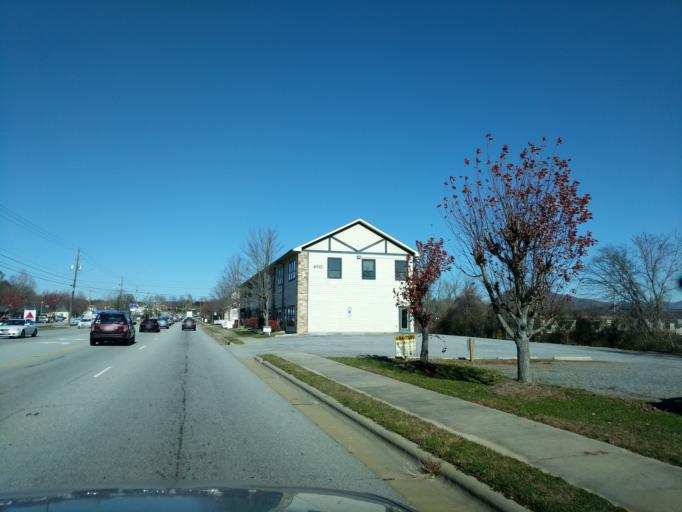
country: US
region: North Carolina
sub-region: Henderson County
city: Fletcher
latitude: 35.4249
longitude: -82.5029
